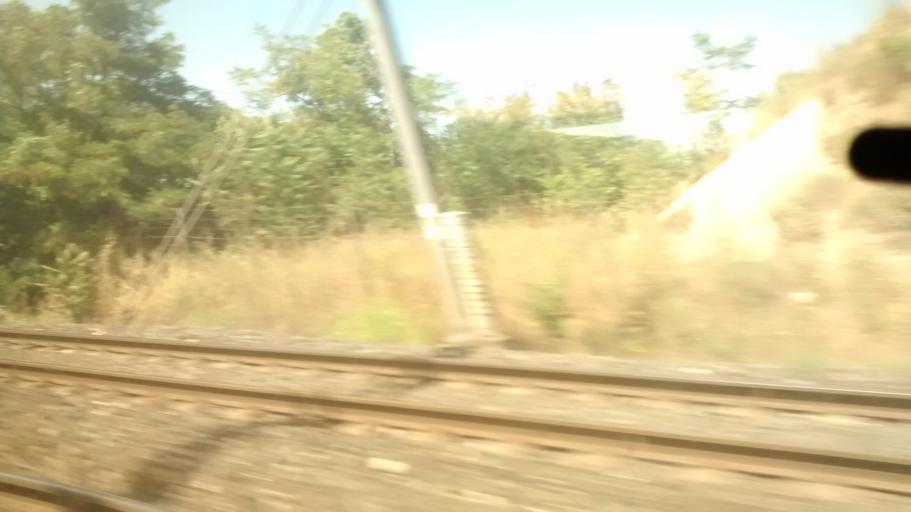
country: FR
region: Languedoc-Roussillon
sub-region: Departement du Gard
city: Redessan
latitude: 43.8221
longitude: 4.4938
